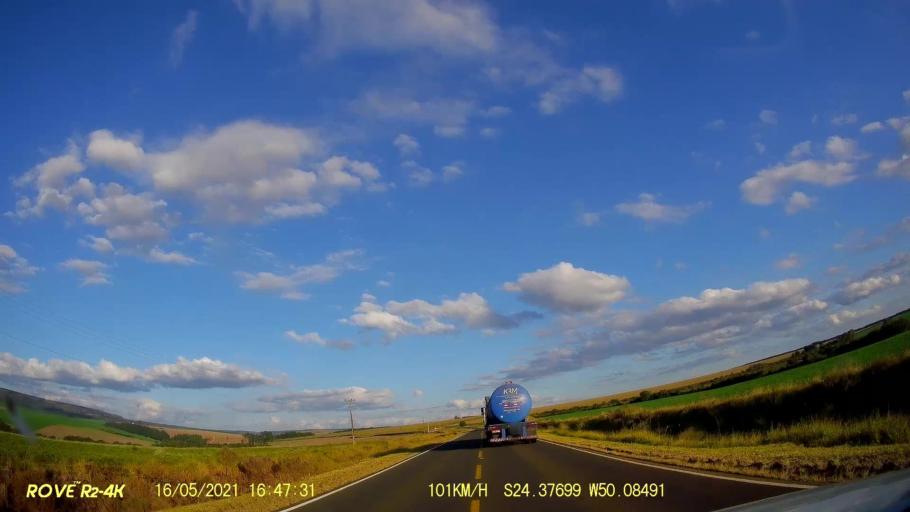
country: BR
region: Parana
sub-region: Pirai Do Sul
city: Pirai do Sul
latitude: -24.3771
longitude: -50.0851
